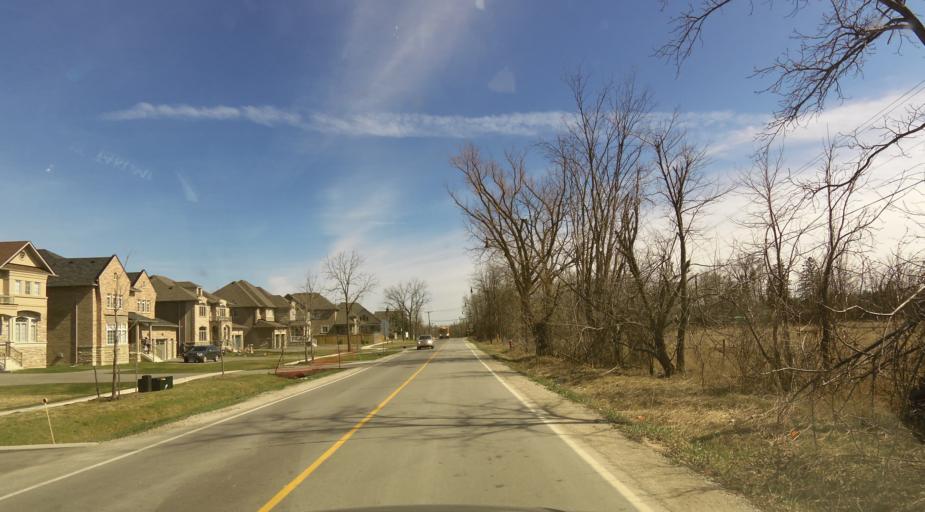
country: CA
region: Ontario
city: Brampton
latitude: 43.6497
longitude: -79.7826
